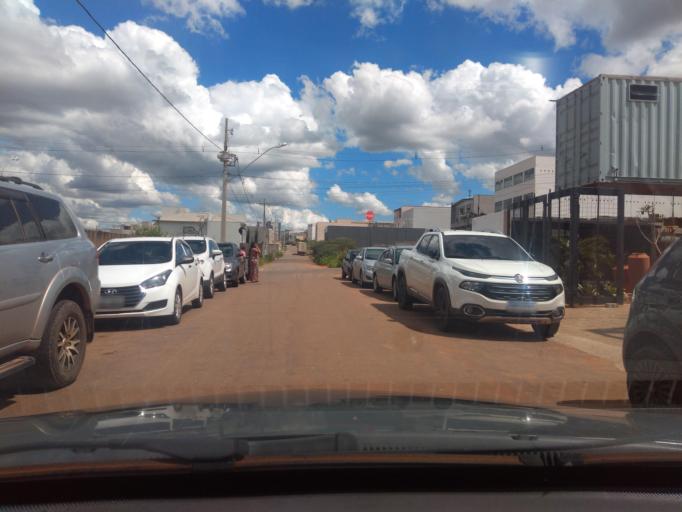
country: BR
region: Minas Gerais
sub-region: Tres Coracoes
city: Tres Coracoes
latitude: -21.6802
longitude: -45.2658
